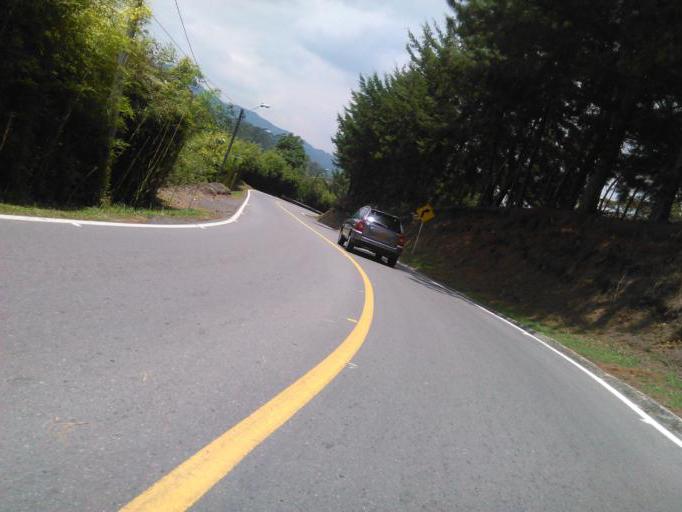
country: CO
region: Antioquia
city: La Ceja
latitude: 6.0202
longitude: -75.4068
